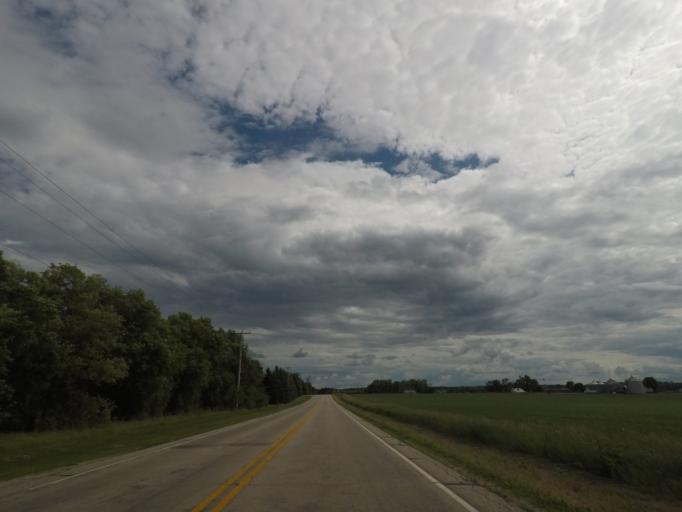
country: US
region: Wisconsin
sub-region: Dane County
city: Belleville
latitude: 42.8324
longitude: -89.5256
